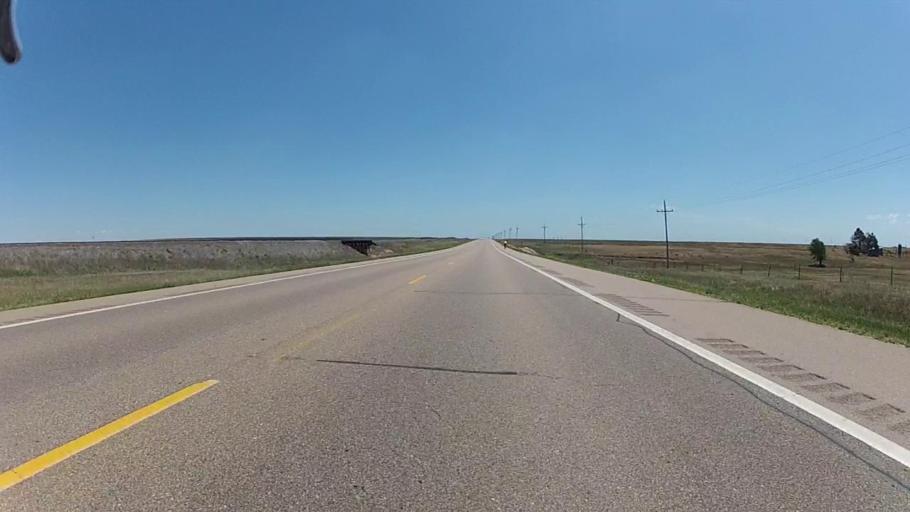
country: US
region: Kansas
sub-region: Ford County
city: Dodge City
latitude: 37.7098
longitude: -100.1199
